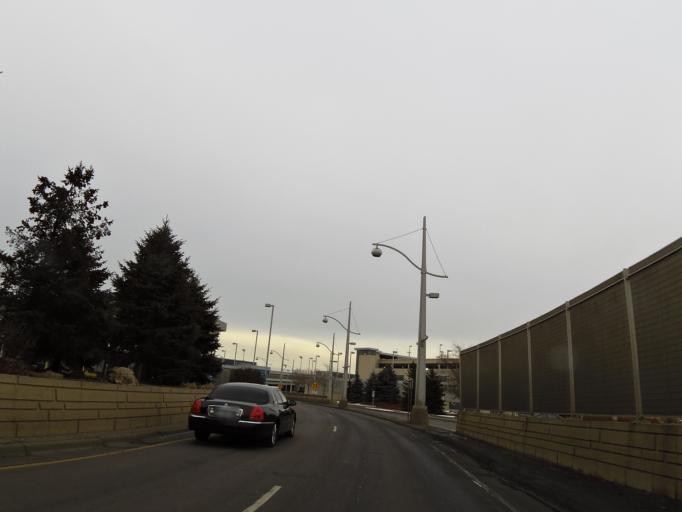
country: US
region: Minnesota
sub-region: Dakota County
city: Mendota Heights
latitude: 44.8800
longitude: -93.2051
